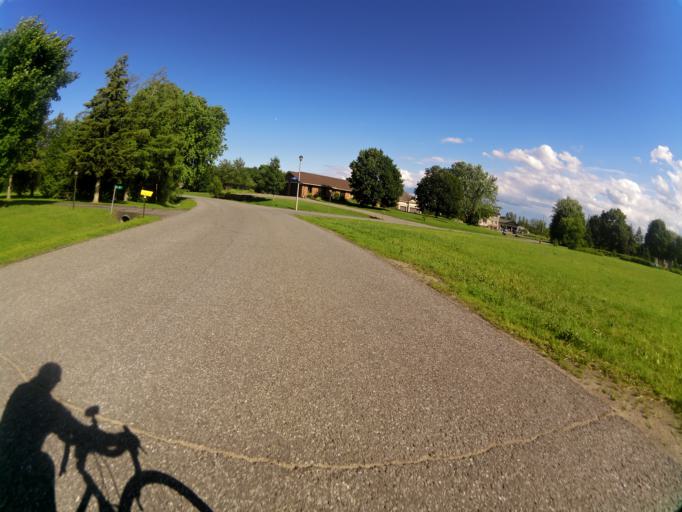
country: CA
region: Ontario
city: Bells Corners
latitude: 45.2623
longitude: -75.8255
